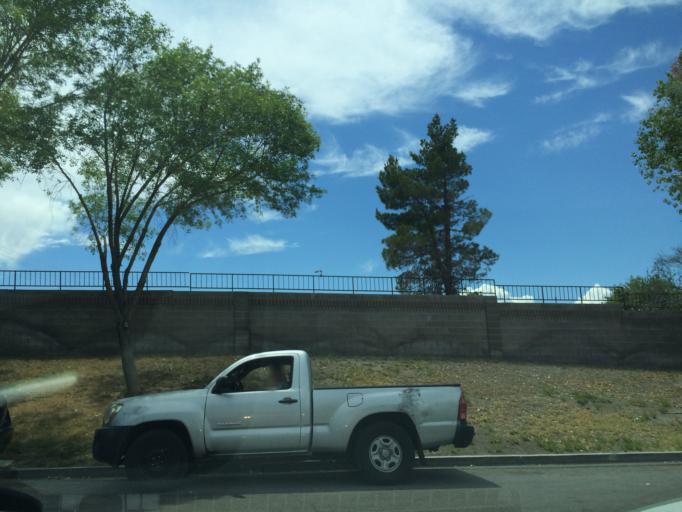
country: US
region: Nevada
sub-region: Clark County
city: North Las Vegas
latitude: 36.2039
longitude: -115.1401
